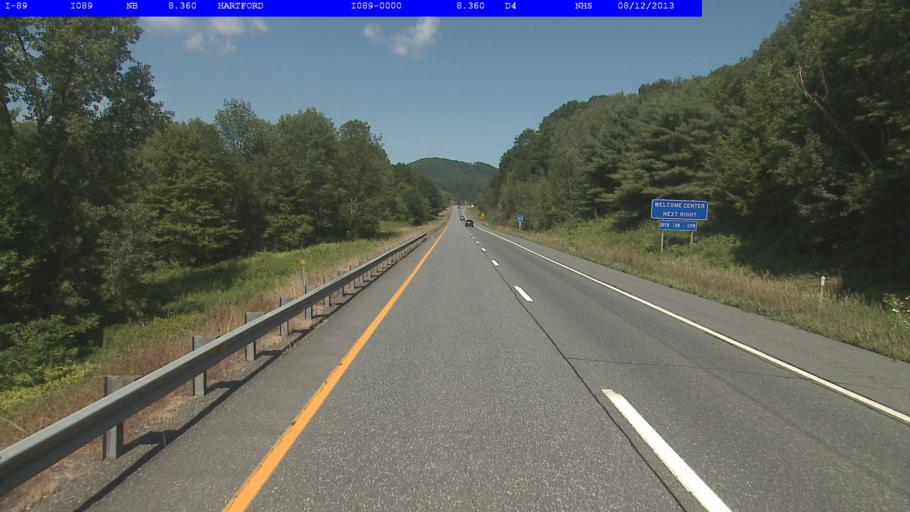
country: US
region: Vermont
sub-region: Windsor County
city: Wilder
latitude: 43.7234
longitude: -72.4186
